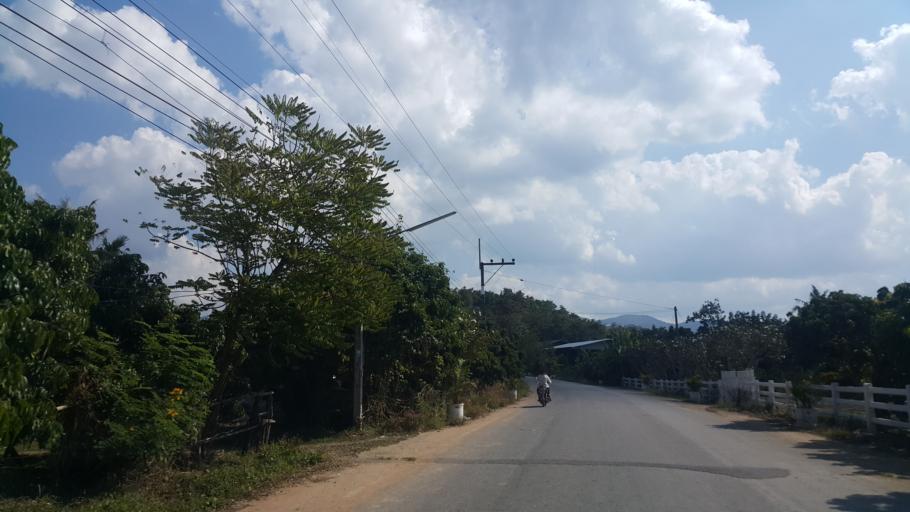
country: TH
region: Lamphun
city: Ban Thi
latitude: 18.6223
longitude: 99.1597
